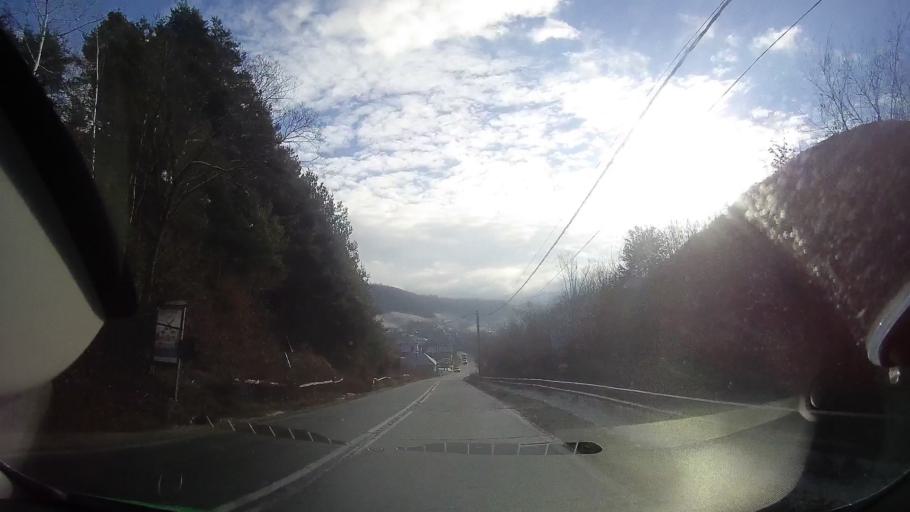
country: RO
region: Alba
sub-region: Comuna Sohodol
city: Sohodol
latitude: 46.3730
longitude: 23.0194
